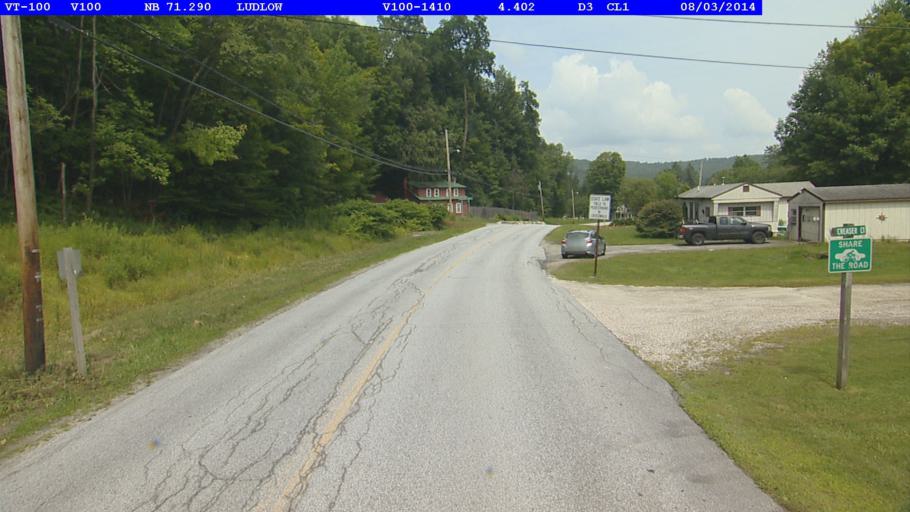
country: US
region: Vermont
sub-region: Windsor County
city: Chester
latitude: 43.3882
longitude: -72.7092
